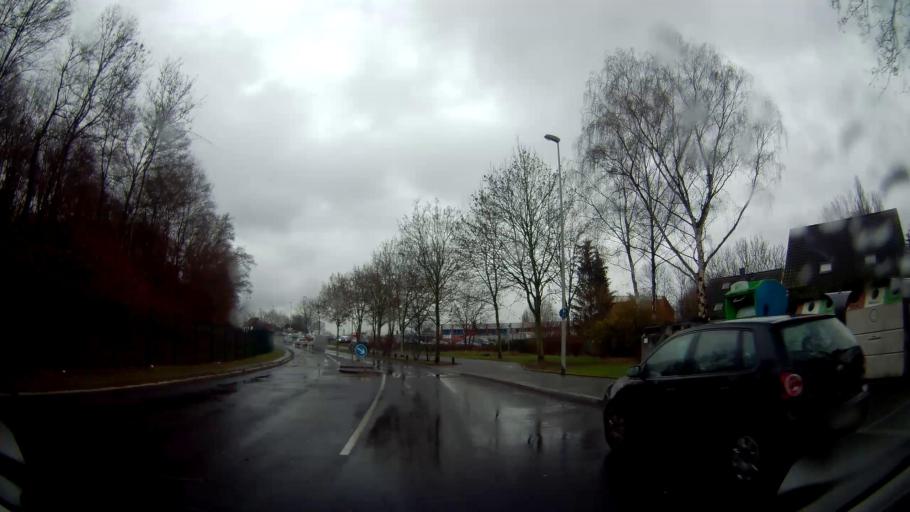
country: DE
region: North Rhine-Westphalia
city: Bochum-Hordel
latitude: 51.5243
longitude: 7.1927
